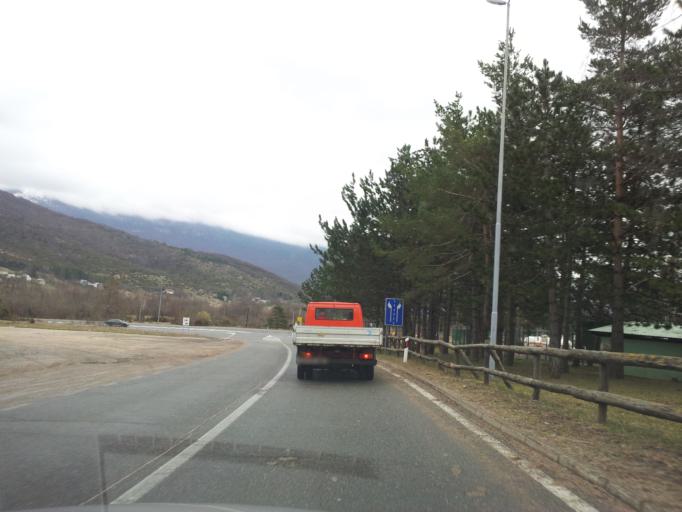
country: HR
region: Licko-Senjska
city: Jezerce
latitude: 44.7660
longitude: 15.6900
